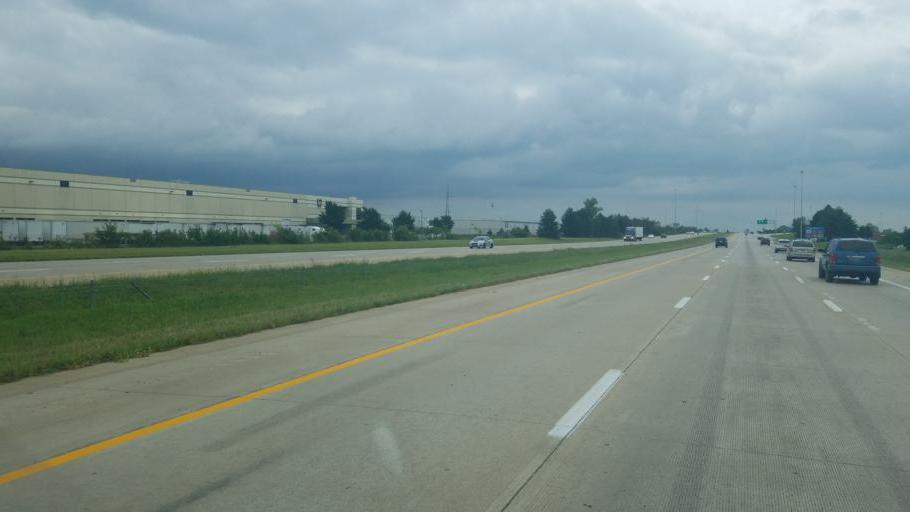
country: US
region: Ohio
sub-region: Franklin County
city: Grove City
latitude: 39.9059
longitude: -83.0872
